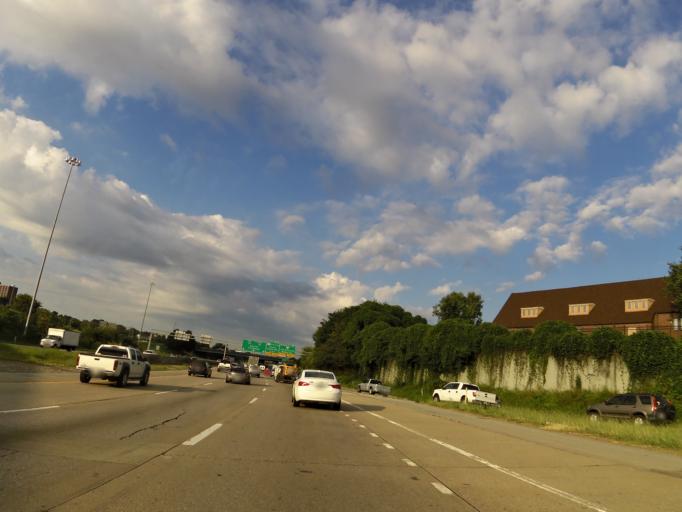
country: US
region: Tennessee
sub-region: Knox County
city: Knoxville
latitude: 35.9682
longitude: -83.9302
